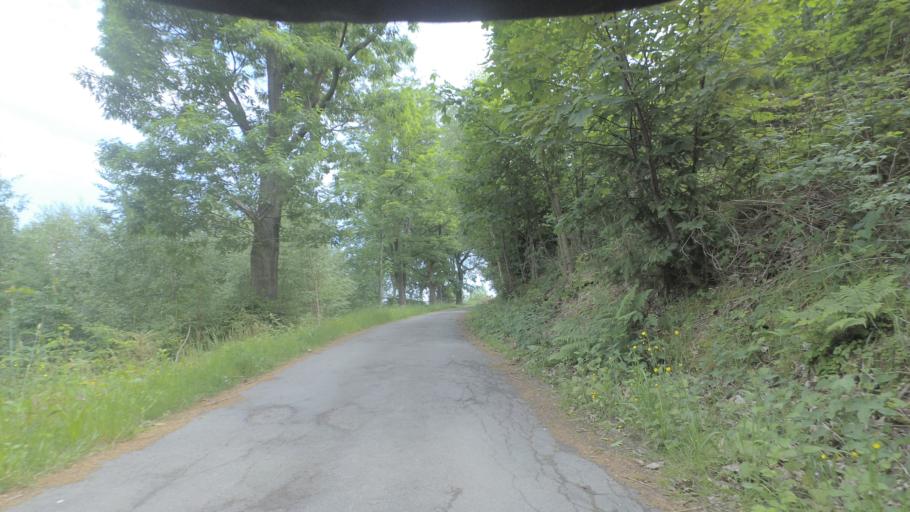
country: DE
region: Lower Saxony
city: Goslar
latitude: 51.8967
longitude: 10.4599
